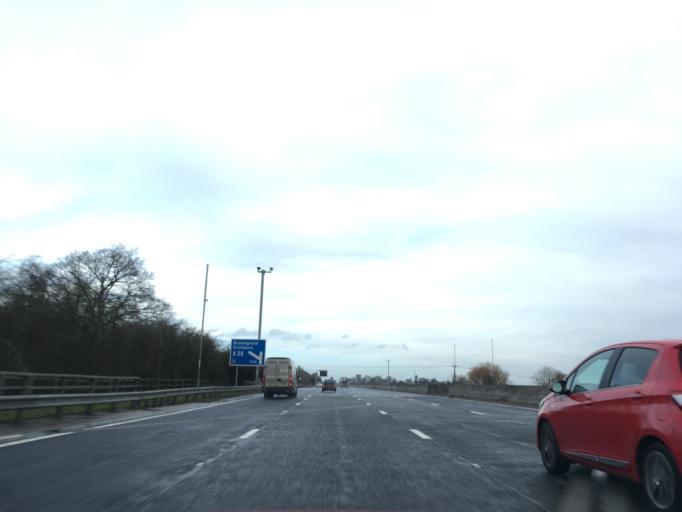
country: GB
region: England
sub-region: Worcestershire
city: Droitwich
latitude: 52.2752
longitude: -2.1219
